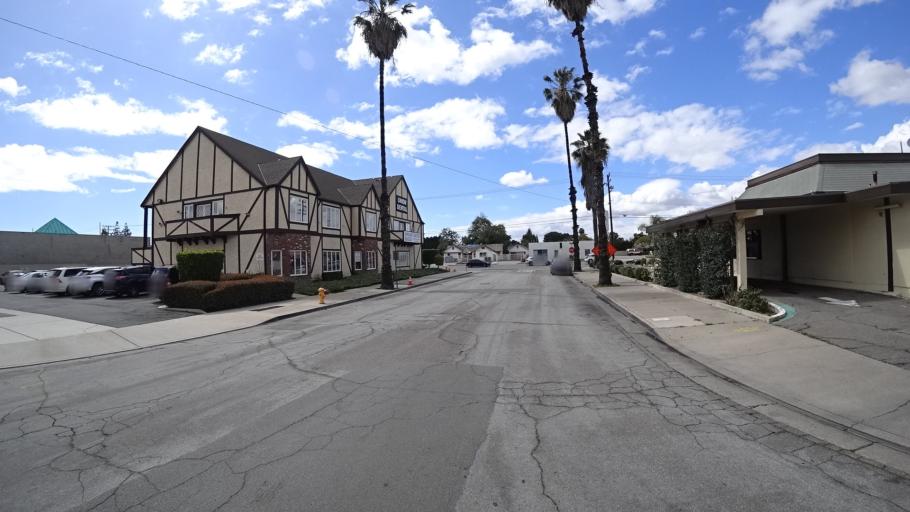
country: US
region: California
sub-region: Orange County
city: Anaheim
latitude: 33.8266
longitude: -117.9408
